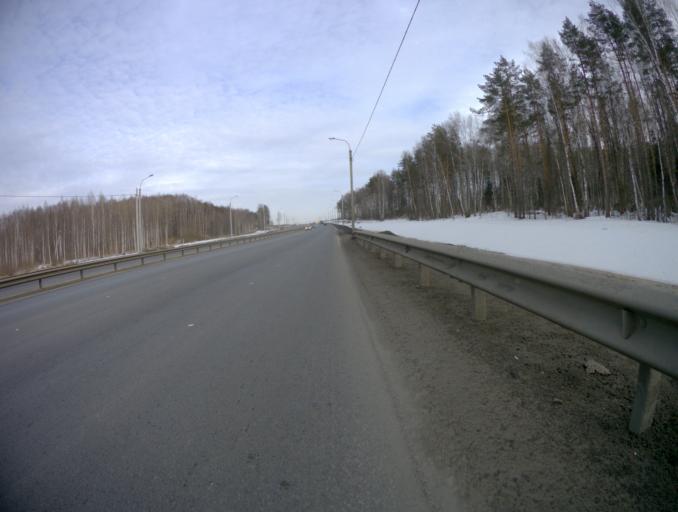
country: RU
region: Vladimir
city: Kommunar
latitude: 56.0751
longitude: 40.4826
